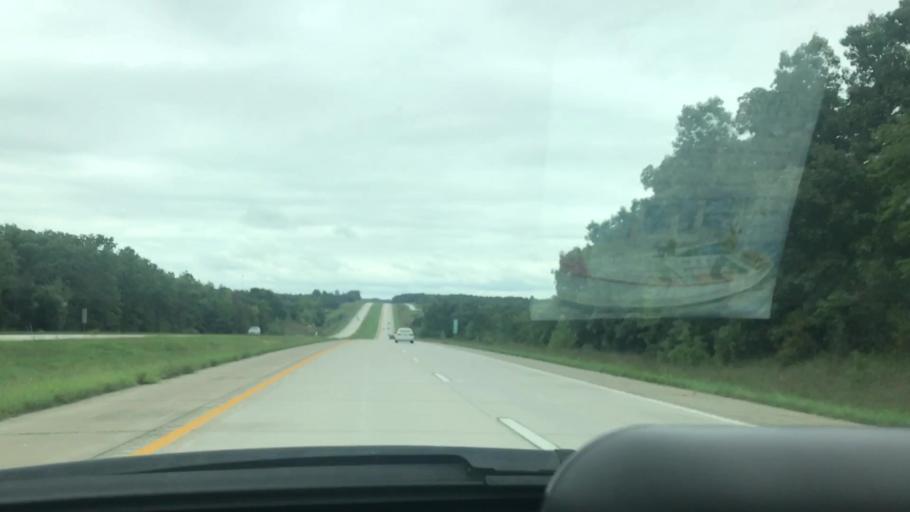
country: US
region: Missouri
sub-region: Dallas County
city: Buffalo
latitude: 37.5435
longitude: -93.1372
